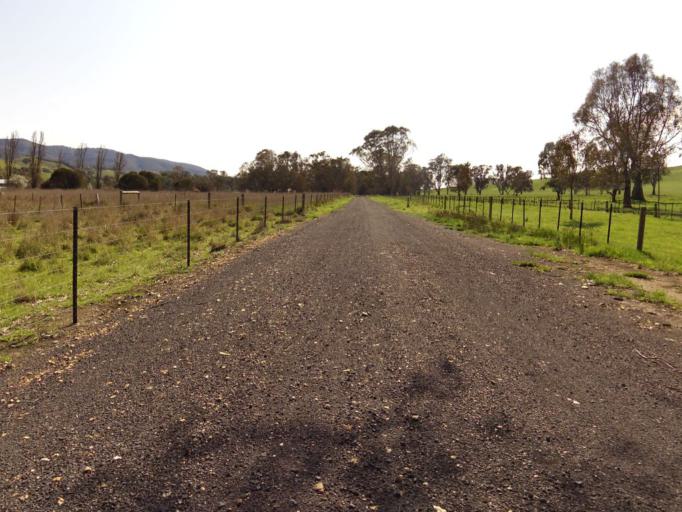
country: AU
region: Victoria
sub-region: Murrindindi
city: Alexandra
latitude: -37.1448
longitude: 145.5885
